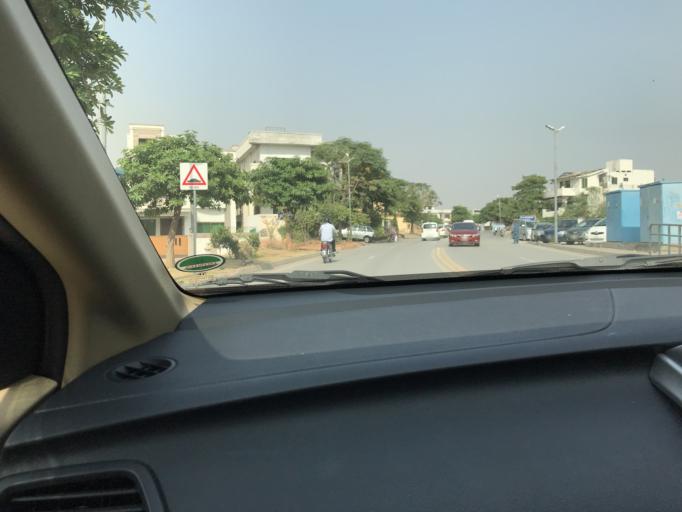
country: PK
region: Punjab
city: Rawalpindi
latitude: 33.5266
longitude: 73.1047
